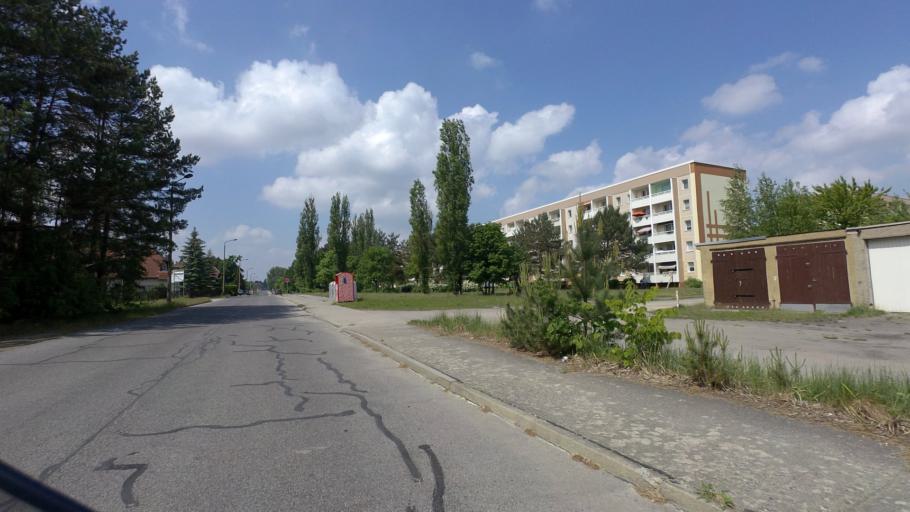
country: DE
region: Saxony
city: Weisswasser
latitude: 51.4925
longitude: 14.6417
